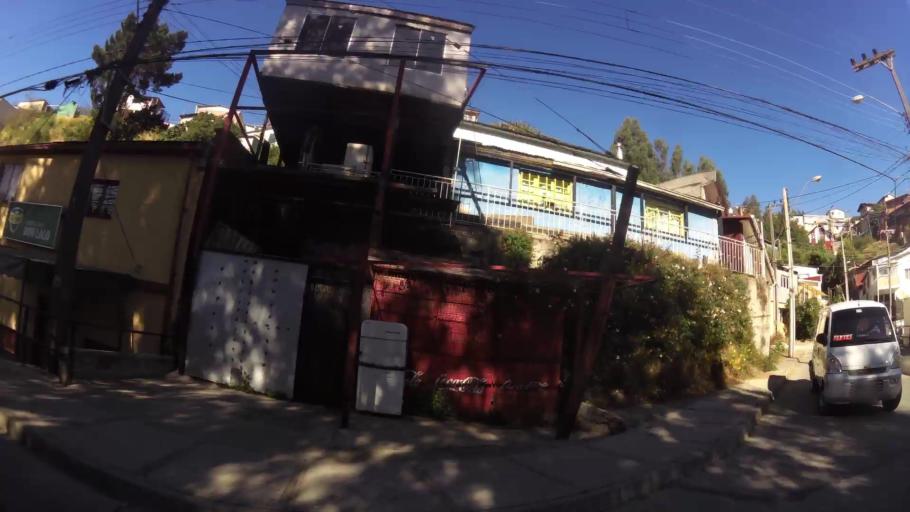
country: CL
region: Valparaiso
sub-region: Provincia de Valparaiso
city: Valparaiso
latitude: -33.0560
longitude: -71.6197
